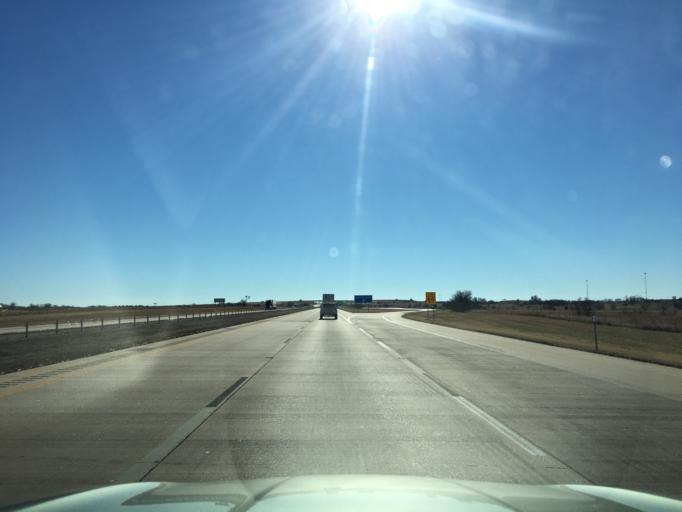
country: US
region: Oklahoma
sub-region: Noble County
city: Perry
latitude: 36.4163
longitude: -97.3272
